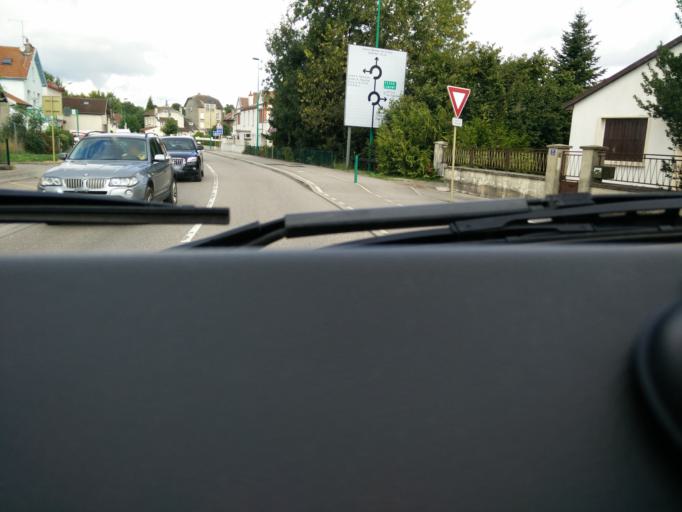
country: FR
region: Lorraine
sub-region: Departement de la Meuse
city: Verdun
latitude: 49.1516
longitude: 5.3972
